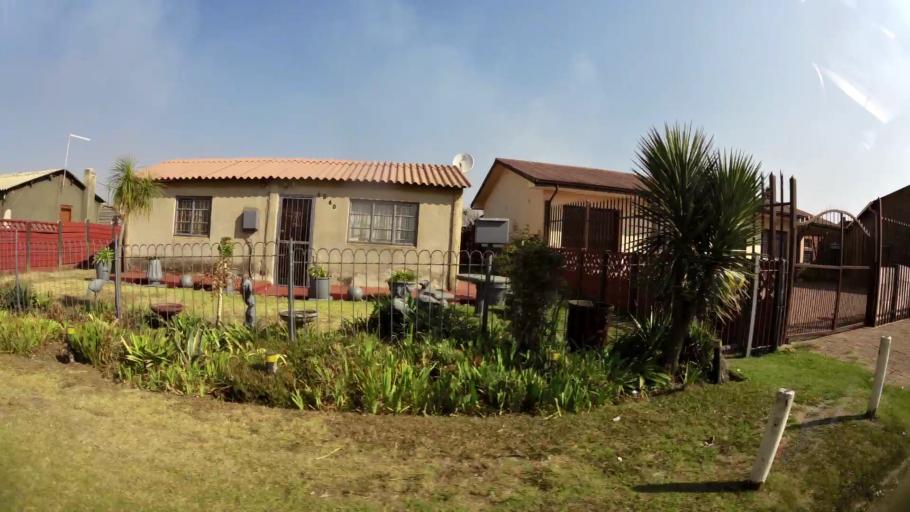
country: ZA
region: Gauteng
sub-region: Ekurhuleni Metropolitan Municipality
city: Brakpan
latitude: -26.1409
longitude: 28.4184
